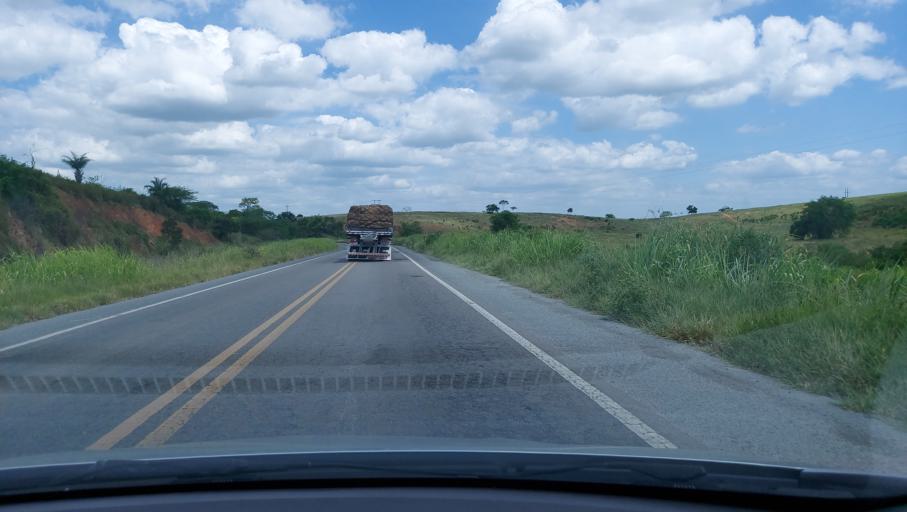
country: BR
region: Bahia
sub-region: Ruy Barbosa
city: Terra Nova
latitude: -12.4447
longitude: -40.7956
